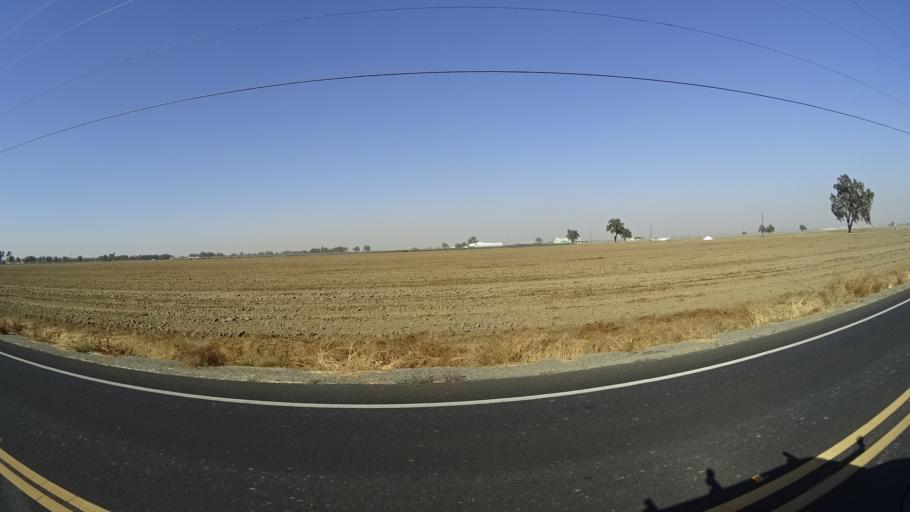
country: US
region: California
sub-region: Yolo County
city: Woodland
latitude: 38.7352
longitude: -121.7671
